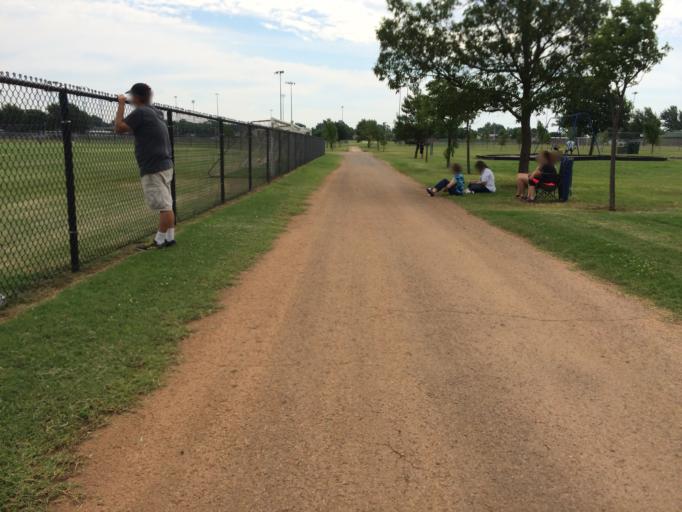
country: US
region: Oklahoma
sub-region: Cleveland County
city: Norman
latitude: 35.2348
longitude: -97.4278
